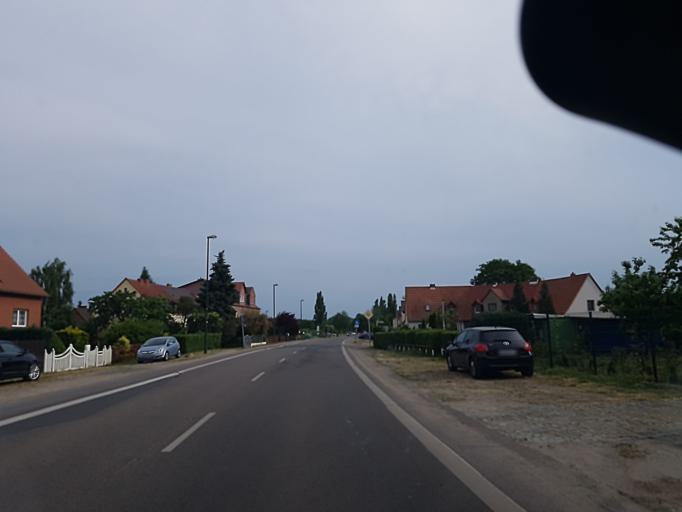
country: DE
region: Saxony-Anhalt
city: Wittenburg
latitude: 51.8678
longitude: 12.6766
